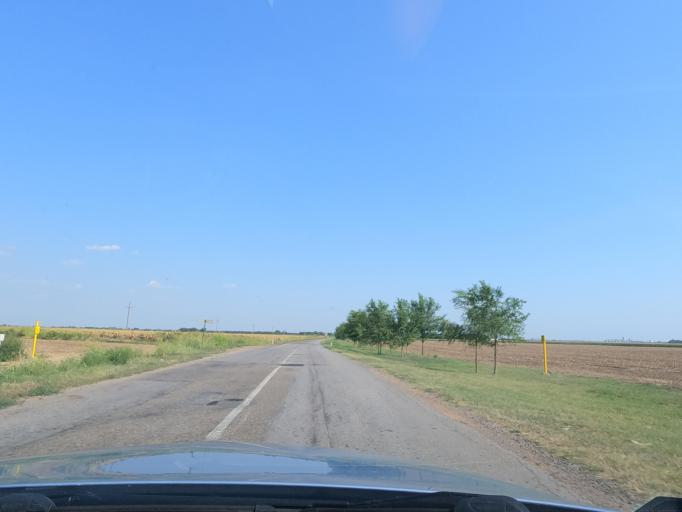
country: RS
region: Autonomna Pokrajina Vojvodina
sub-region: Juznobacki Okrug
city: Becej
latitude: 45.6414
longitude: 19.9949
